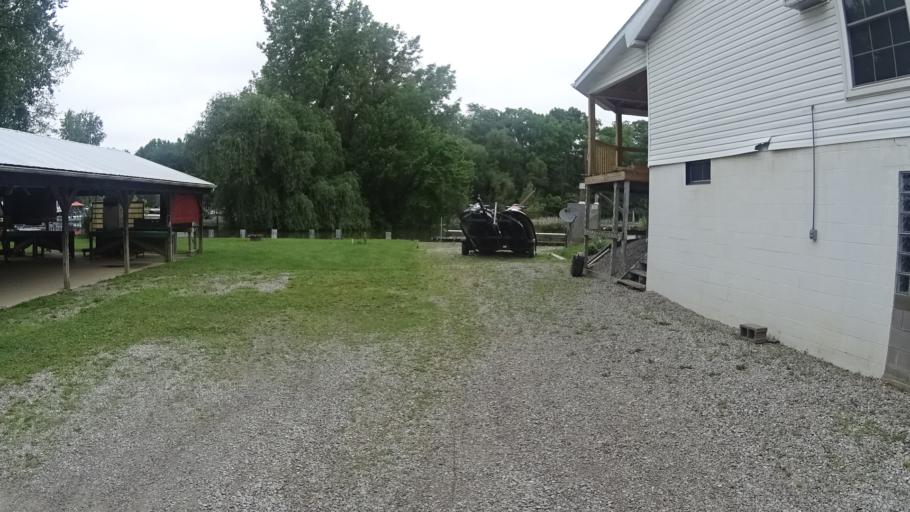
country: US
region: Ohio
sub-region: Erie County
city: Huron
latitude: 41.3545
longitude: -82.5575
